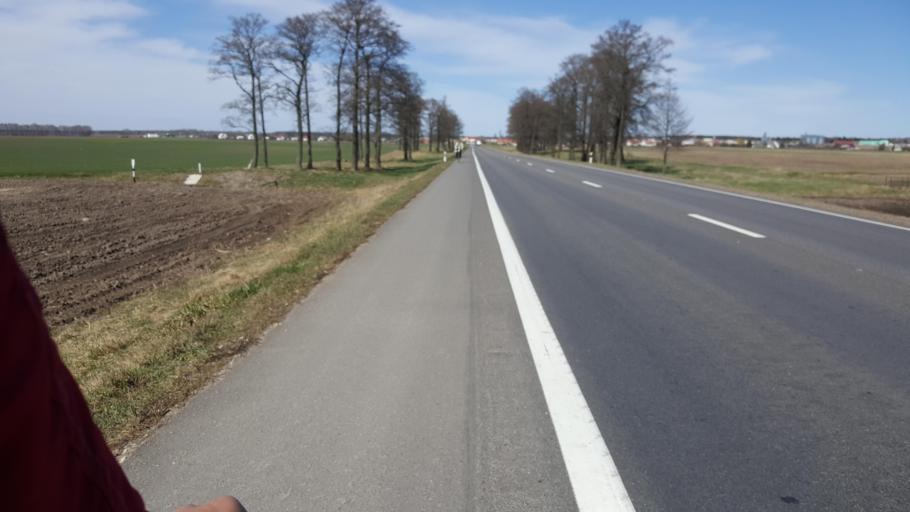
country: BY
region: Brest
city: Kamyanyets
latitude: 52.3144
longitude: 23.7810
